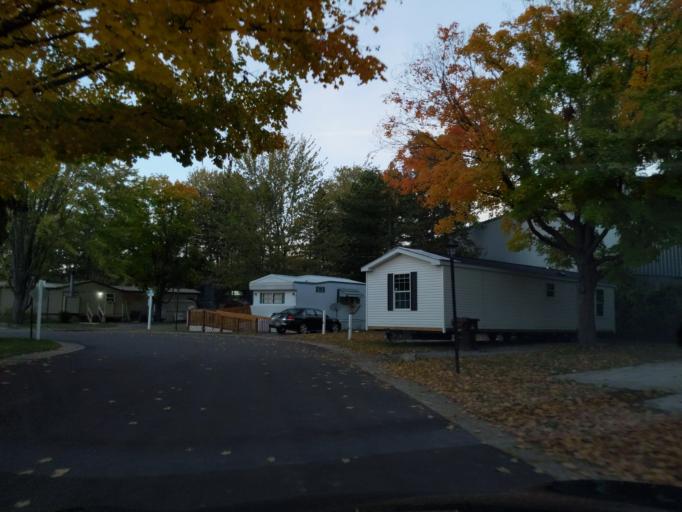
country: US
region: Michigan
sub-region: Ingham County
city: Edgemont Park
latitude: 42.7252
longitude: -84.5972
